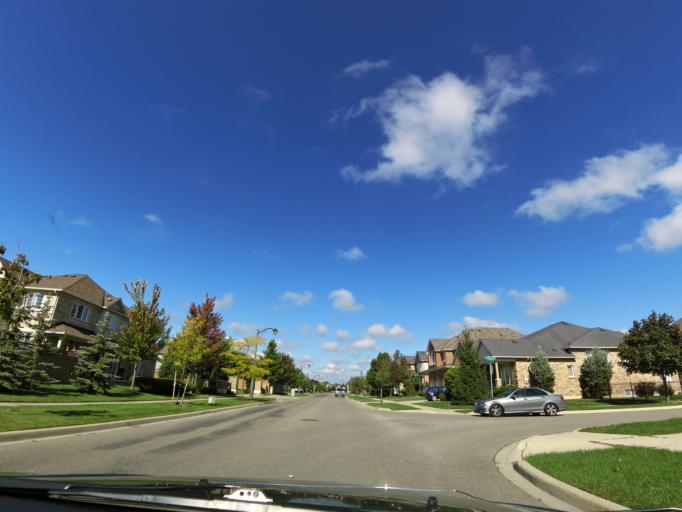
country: CA
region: Ontario
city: Burlington
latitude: 43.3957
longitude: -79.8123
